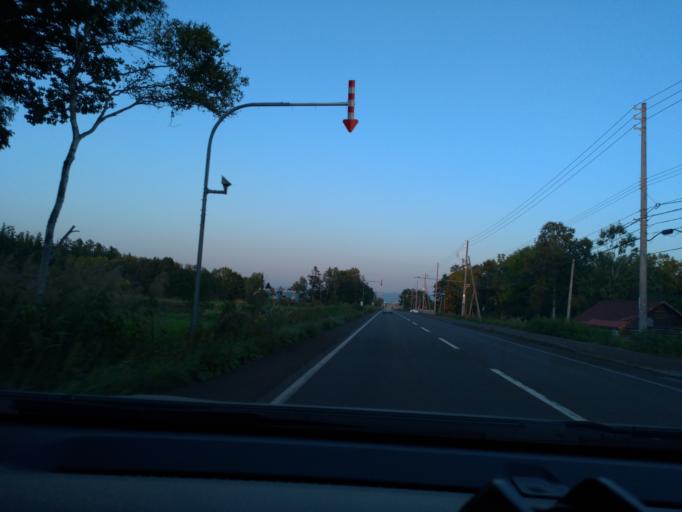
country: JP
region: Hokkaido
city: Tobetsu
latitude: 43.3272
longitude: 141.6401
